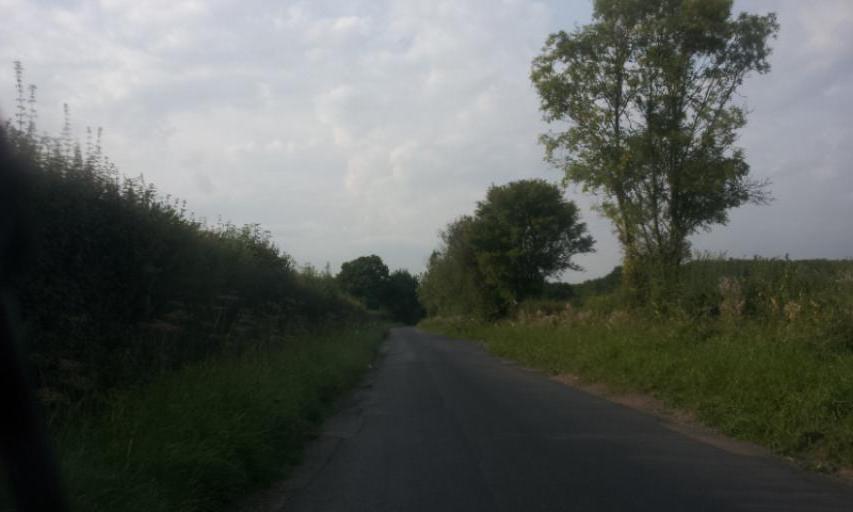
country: GB
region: England
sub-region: Kent
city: Yalding
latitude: 51.1950
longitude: 0.4161
